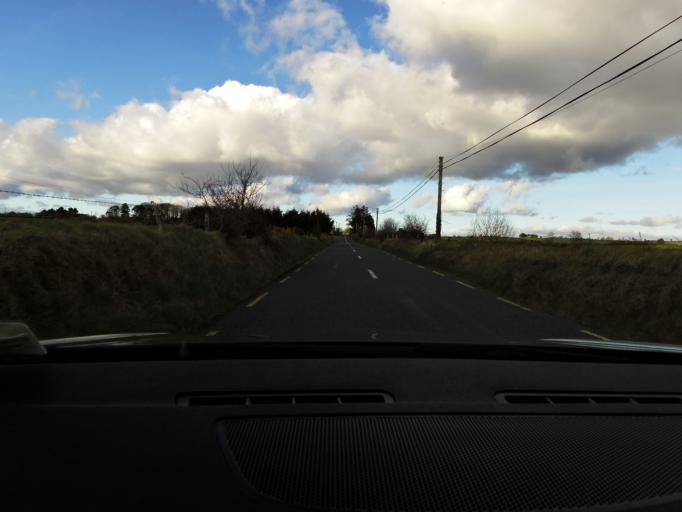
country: IE
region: Connaught
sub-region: Roscommon
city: Castlerea
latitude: 53.6670
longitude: -8.5017
